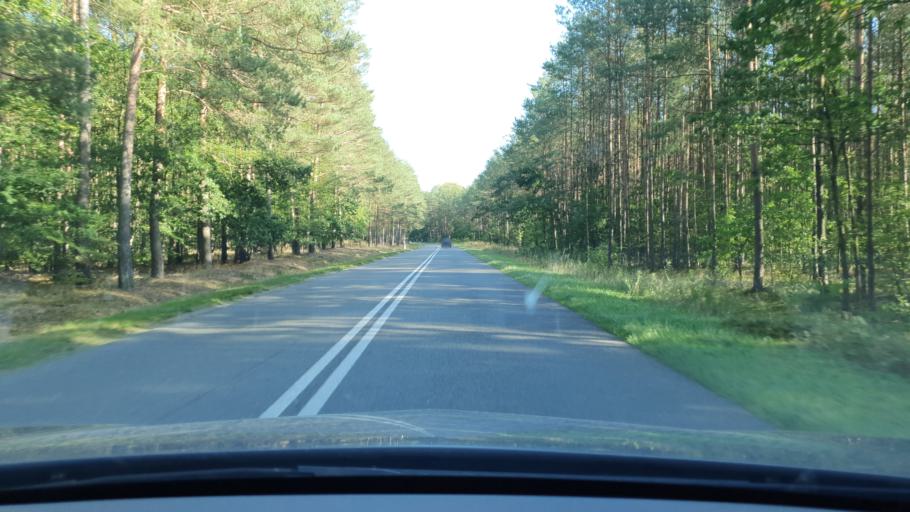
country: PL
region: West Pomeranian Voivodeship
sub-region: Powiat goleniowski
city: Przybiernow
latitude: 53.8239
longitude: 14.8074
